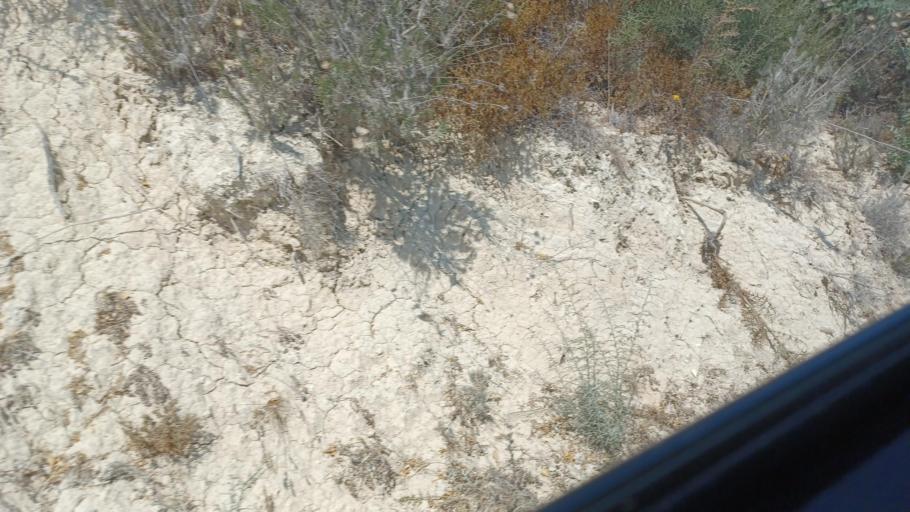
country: CY
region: Pafos
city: Mesogi
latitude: 34.8473
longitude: 32.4672
